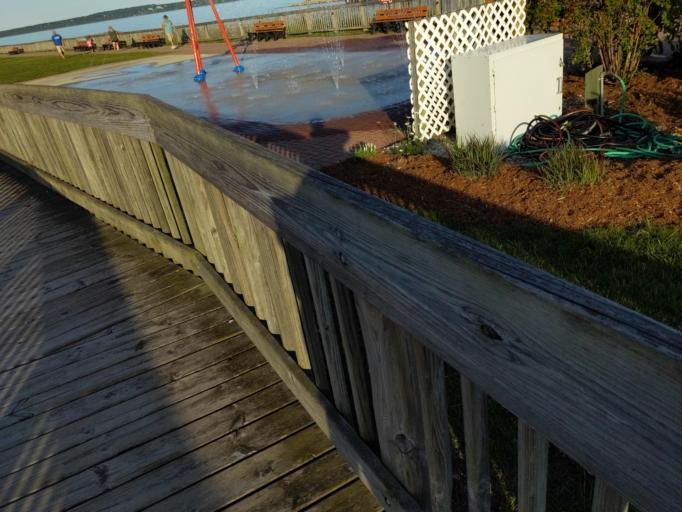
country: US
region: Michigan
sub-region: Mackinac County
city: Saint Ignace
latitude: 45.8653
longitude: -84.7182
